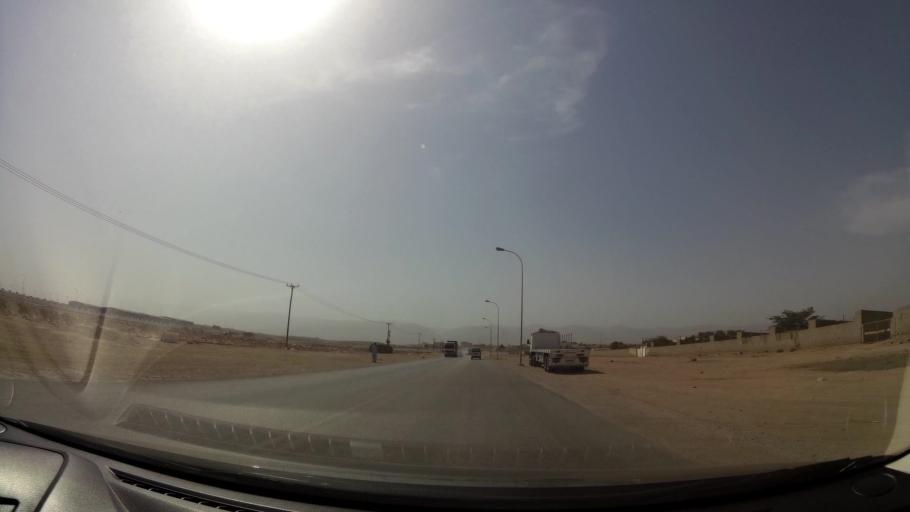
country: OM
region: Zufar
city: Salalah
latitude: 16.9873
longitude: 54.0155
